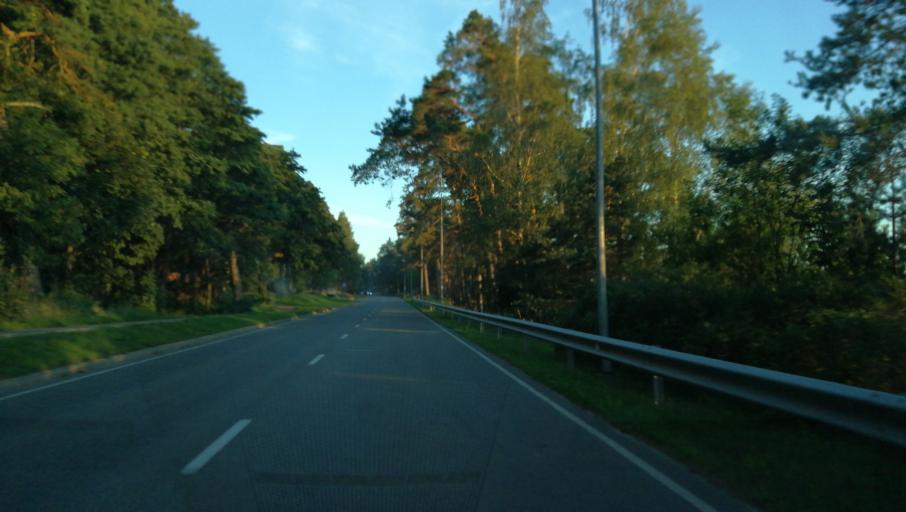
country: LV
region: Saulkrastu
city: Saulkrasti
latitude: 57.2872
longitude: 24.4130
